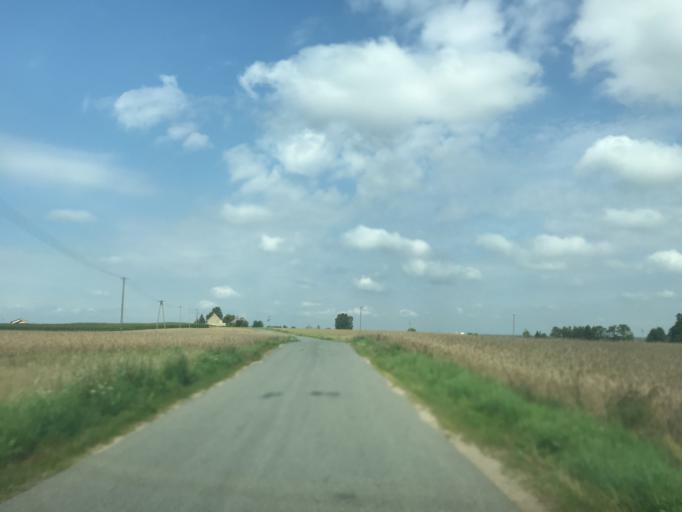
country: PL
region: Warmian-Masurian Voivodeship
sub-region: Powiat nowomiejski
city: Kurzetnik
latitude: 53.3985
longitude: 19.4713
